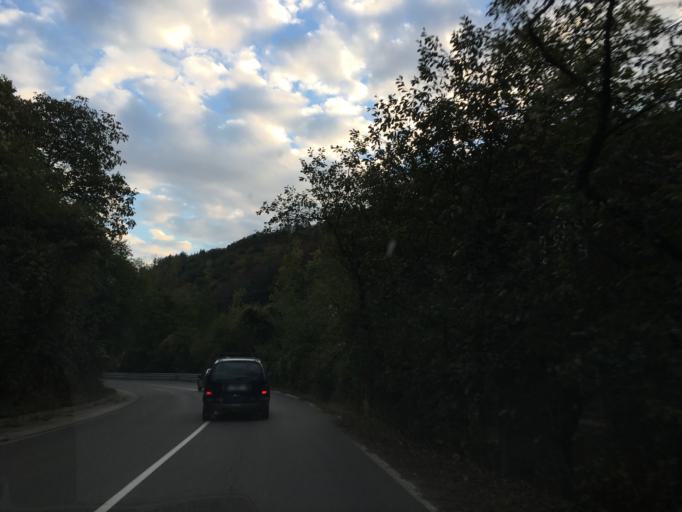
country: BG
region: Sofiya
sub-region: Obshtina Svoge
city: Svoge
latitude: 42.8955
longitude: 23.3893
